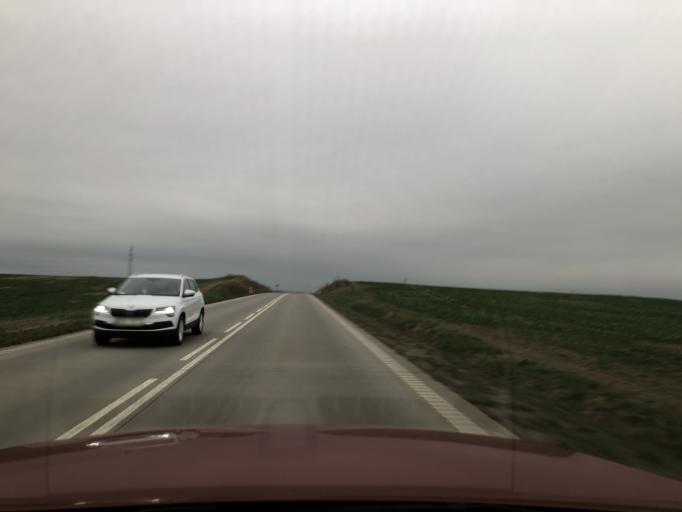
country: PL
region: Lower Silesian Voivodeship
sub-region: Powiat swidnicki
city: Zarow
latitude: 50.9000
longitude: 16.4795
